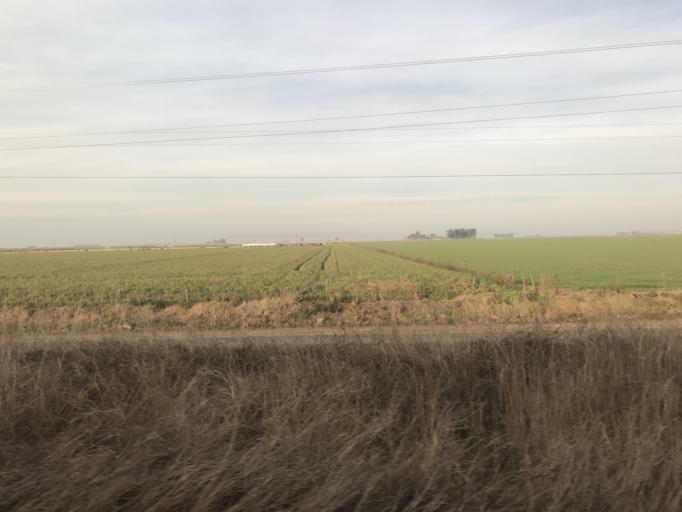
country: AR
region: Cordoba
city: Leones
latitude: -32.6818
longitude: -62.2037
